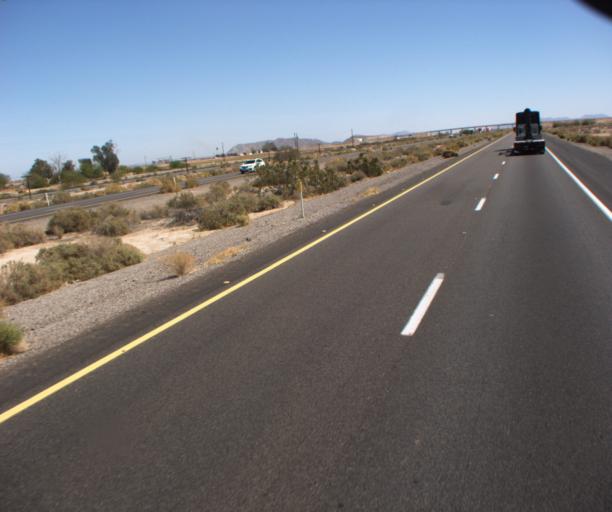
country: US
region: Arizona
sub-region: Yuma County
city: Wellton
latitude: 32.6733
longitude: -114.0854
